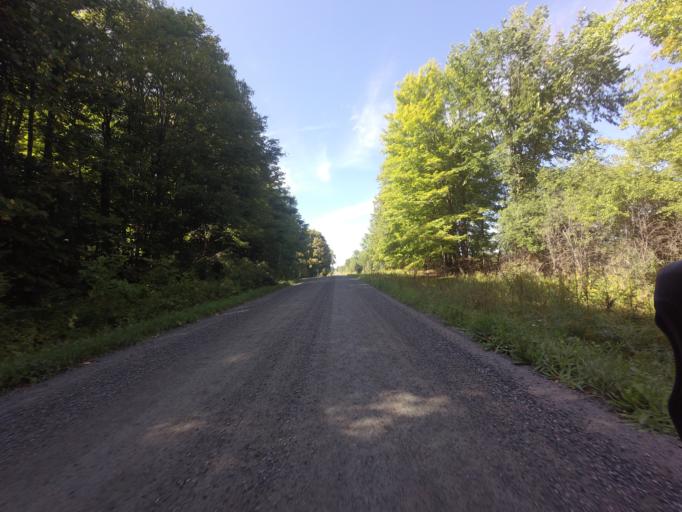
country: CA
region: Ontario
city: Perth
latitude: 44.9607
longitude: -76.3385
